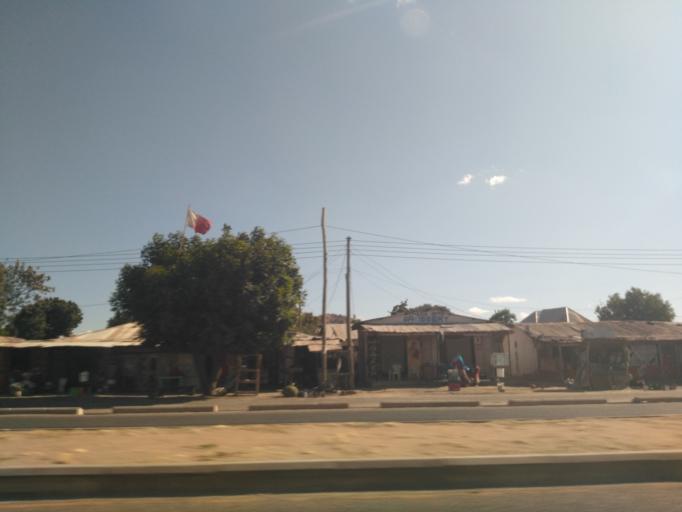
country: TZ
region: Dodoma
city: Dodoma
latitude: -6.1665
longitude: 35.7222
